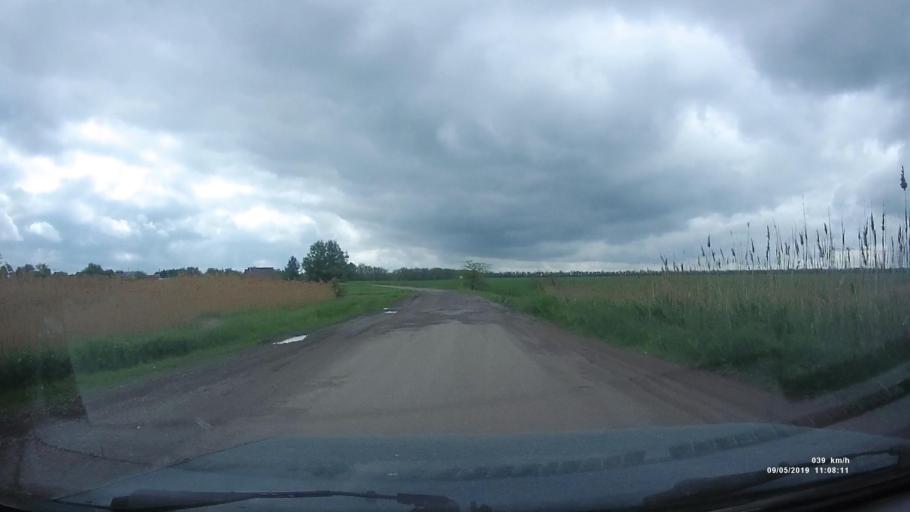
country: RU
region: Krasnodarskiy
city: Kanelovskaya
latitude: 46.7907
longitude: 39.2091
